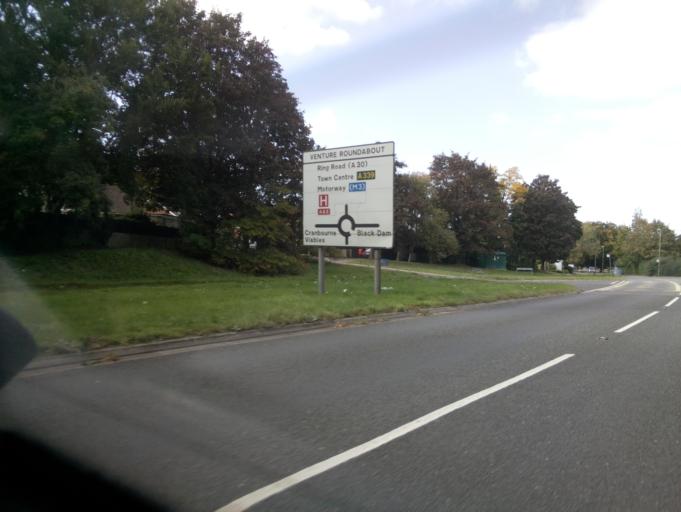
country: GB
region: England
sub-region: Hampshire
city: Basingstoke
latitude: 51.2528
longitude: -1.0787
